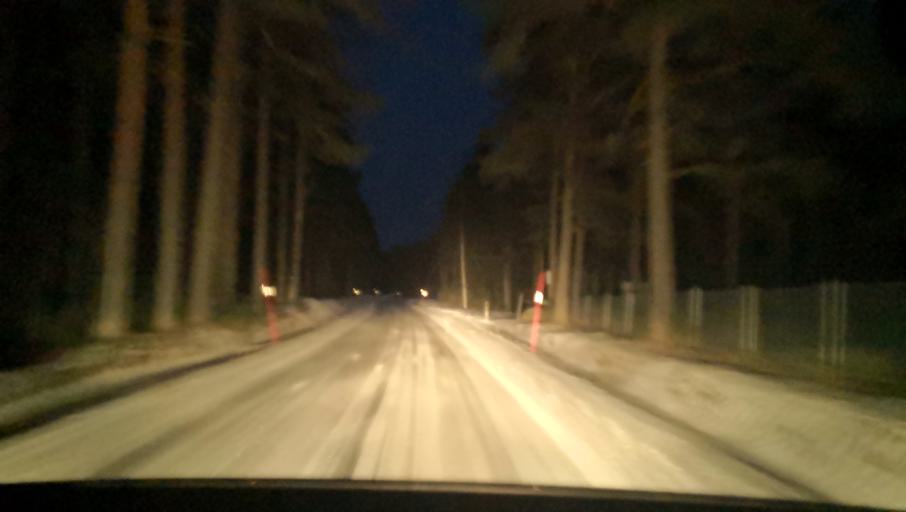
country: SE
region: Uppsala
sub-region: Heby Kommun
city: Tarnsjo
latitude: 60.2861
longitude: 16.8067
